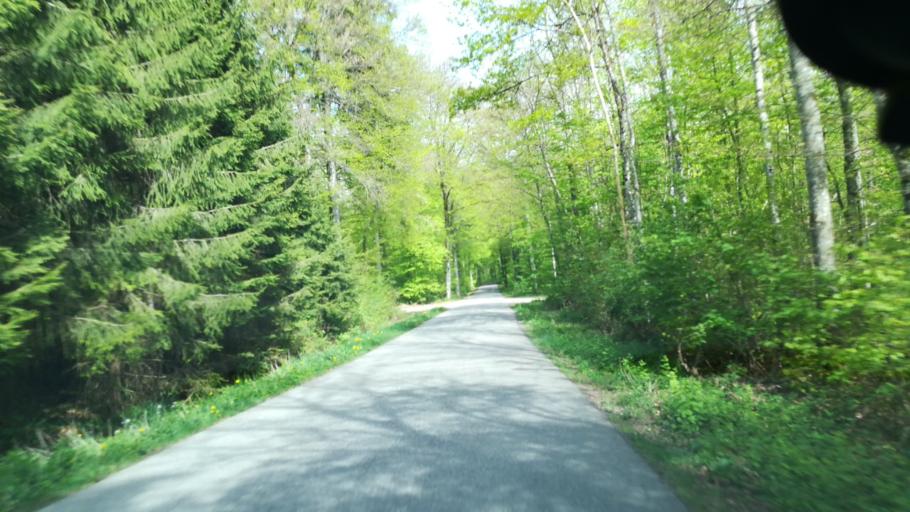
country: CH
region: Thurgau
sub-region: Kreuzlingen District
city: Ermatingen
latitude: 47.6455
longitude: 9.0787
